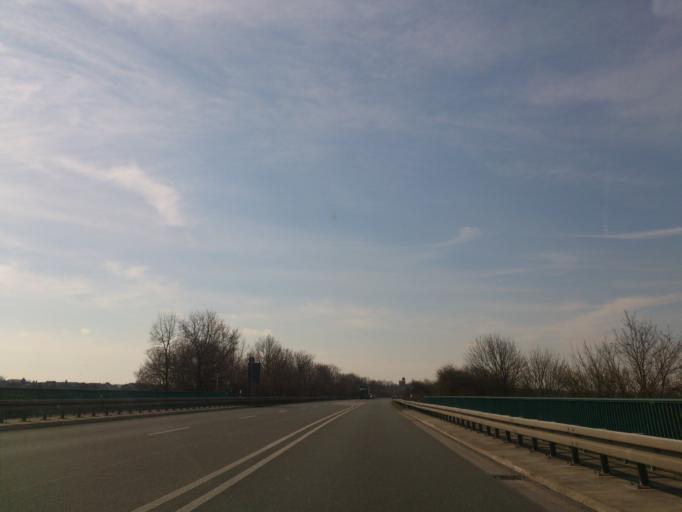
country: DE
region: North Rhine-Westphalia
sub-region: Regierungsbezirk Detmold
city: Salzkotten
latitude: 51.6490
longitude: 8.6571
